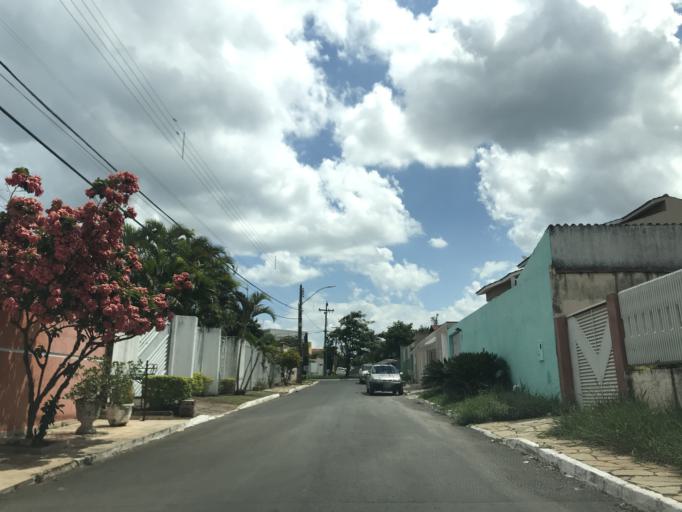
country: BR
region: Federal District
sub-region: Brasilia
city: Brasilia
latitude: -15.6834
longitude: -47.8352
